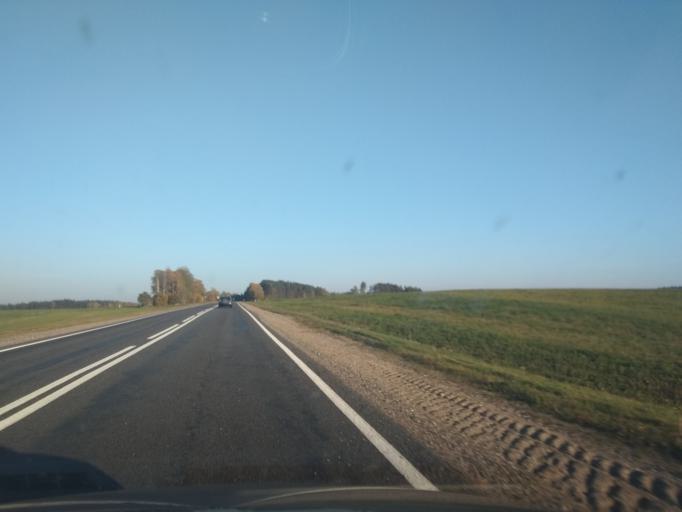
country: BY
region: Grodnenskaya
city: Zel'va
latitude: 53.1405
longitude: 24.6982
